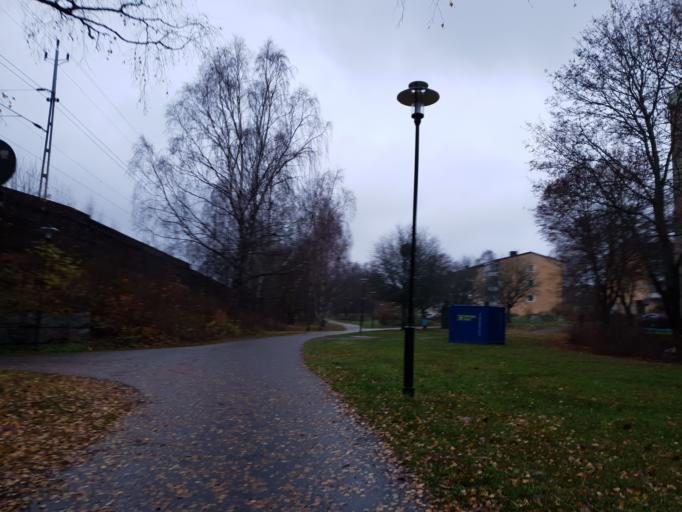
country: SE
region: Stockholm
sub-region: Stockholms Kommun
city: Arsta
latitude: 59.2410
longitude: 18.0858
